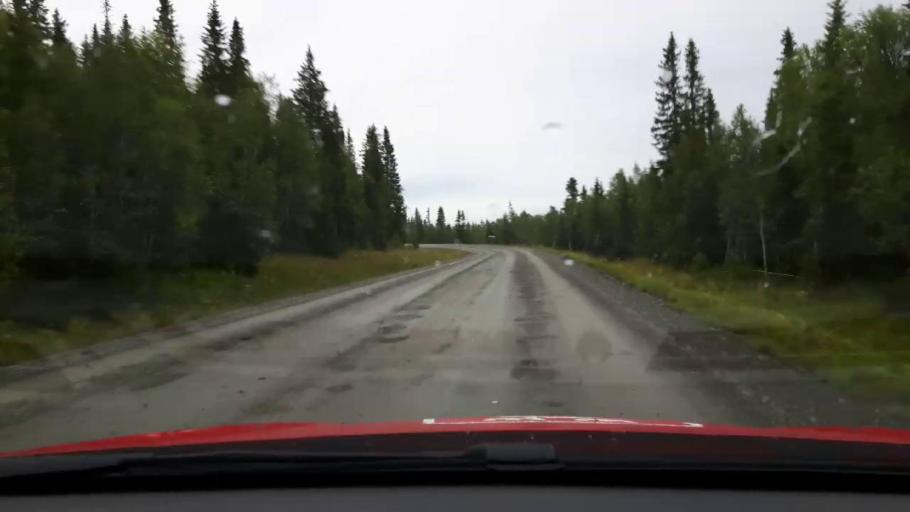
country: SE
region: Jaemtland
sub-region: Are Kommun
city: Are
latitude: 63.4700
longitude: 12.5968
